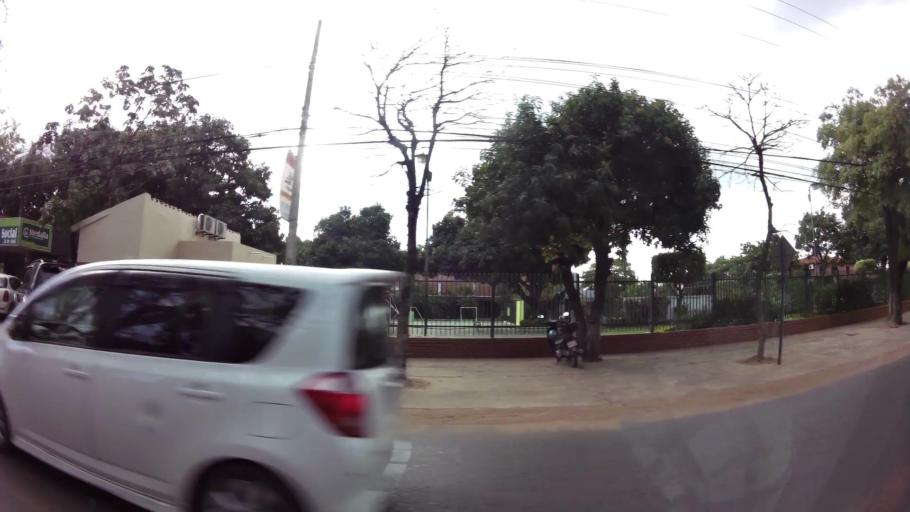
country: PY
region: Central
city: Villa Elisa
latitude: -25.3414
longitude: -57.5657
